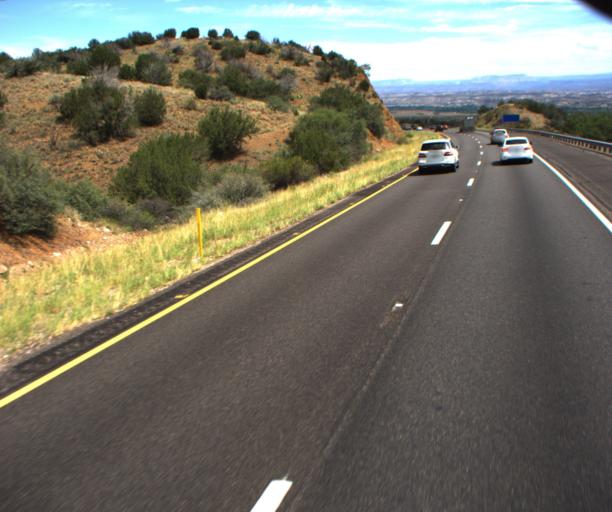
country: US
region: Arizona
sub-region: Yavapai County
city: Camp Verde
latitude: 34.5415
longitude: -111.9069
